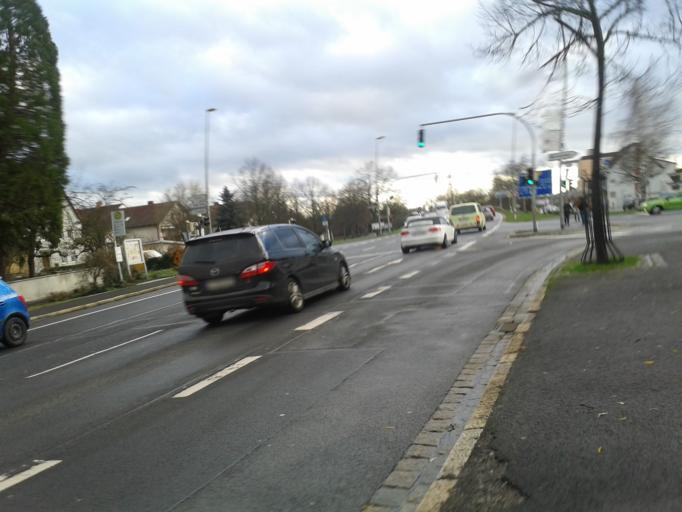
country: DE
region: Bavaria
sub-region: Upper Franconia
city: Hallstadt
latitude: 49.9242
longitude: 10.8743
